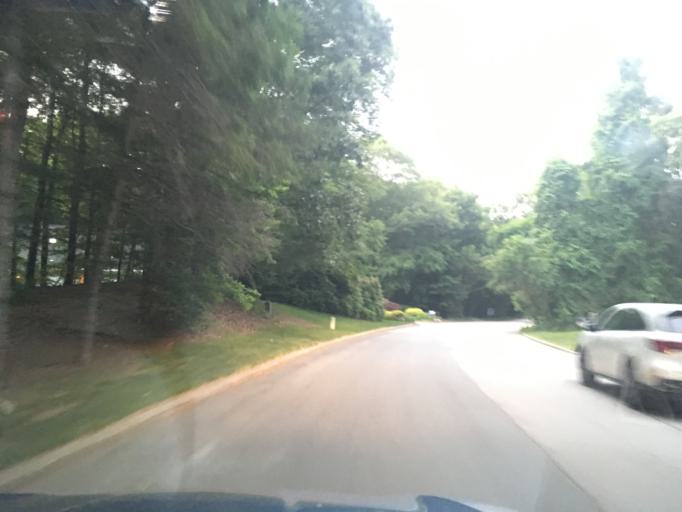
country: US
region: Rhode Island
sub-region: Washington County
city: Exeter
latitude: 41.6286
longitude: -71.5188
